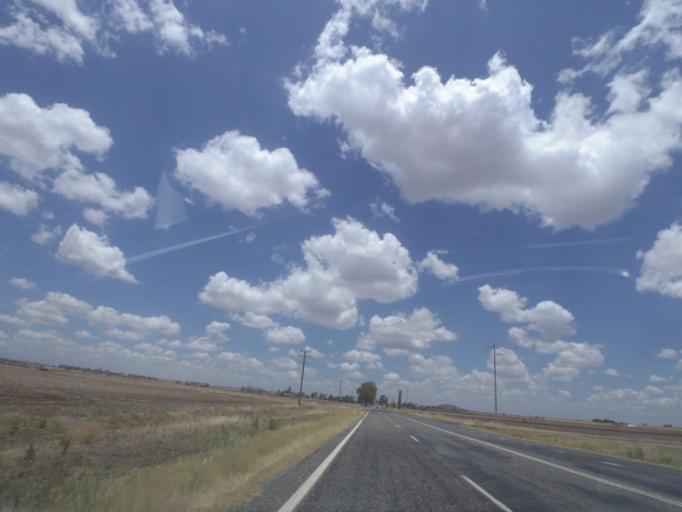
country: AU
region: Queensland
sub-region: Toowoomba
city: Top Camp
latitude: -27.9217
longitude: 151.9831
